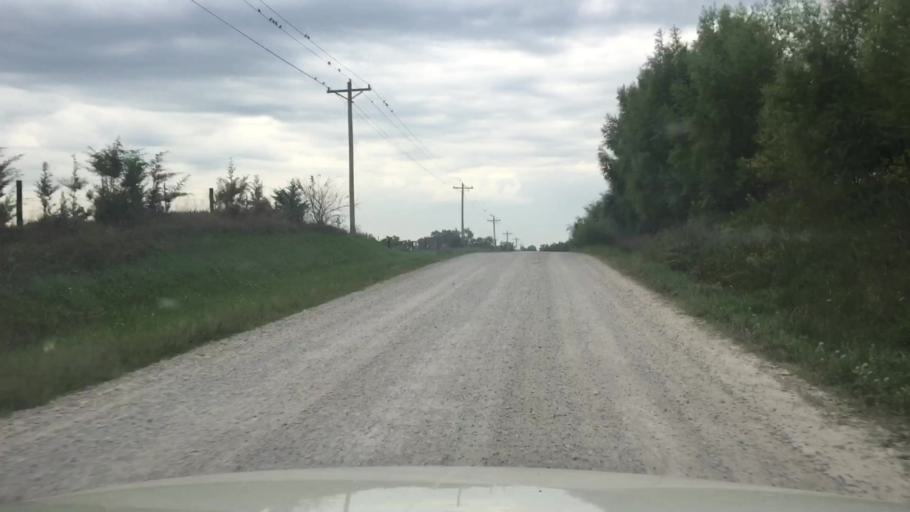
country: US
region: Iowa
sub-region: Story County
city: Huxley
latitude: 41.8967
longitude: -93.5810
